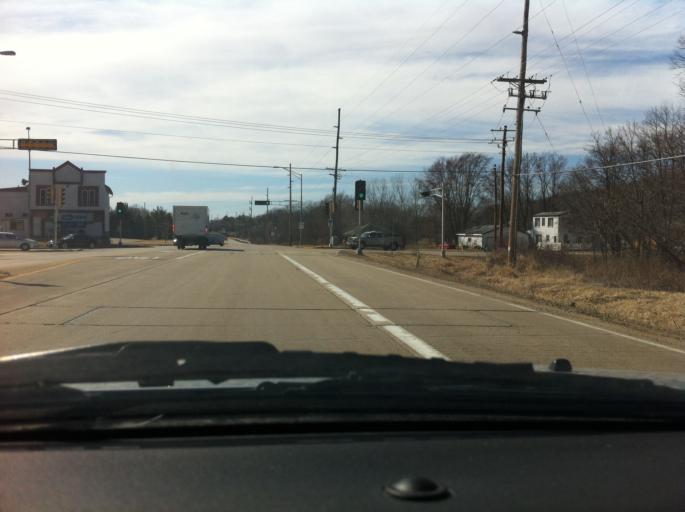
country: US
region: Wisconsin
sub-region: Dane County
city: Windsor
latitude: 43.1939
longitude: -89.2908
